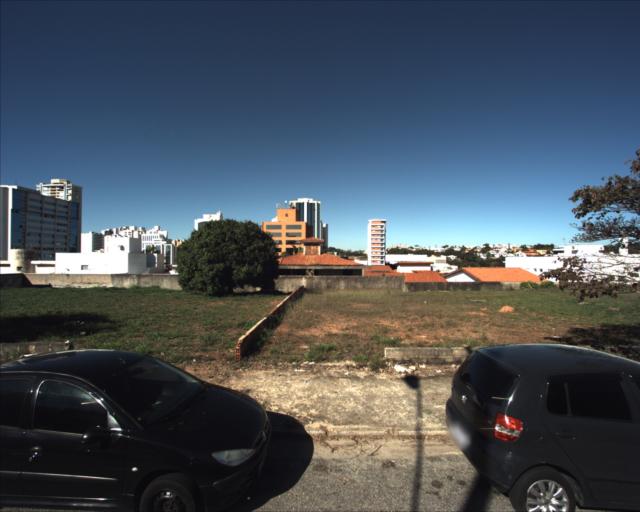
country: BR
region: Sao Paulo
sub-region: Sorocaba
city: Sorocaba
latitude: -23.5214
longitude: -47.4664
